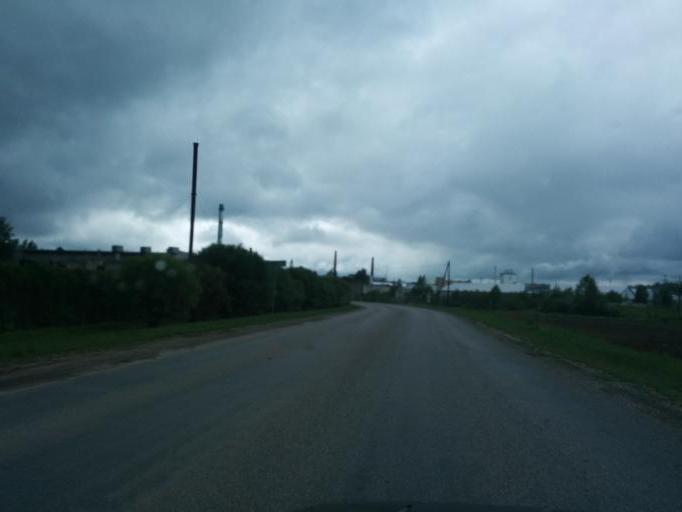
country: LV
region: Valmieras Rajons
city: Valmiera
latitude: 57.5178
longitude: 25.4555
